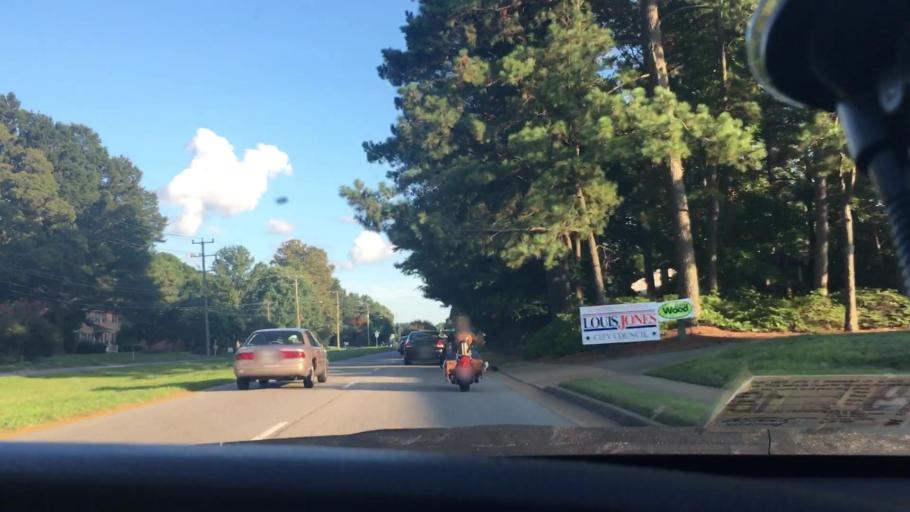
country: US
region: Virginia
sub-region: City of Norfolk
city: Norfolk
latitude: 36.8874
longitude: -76.1366
